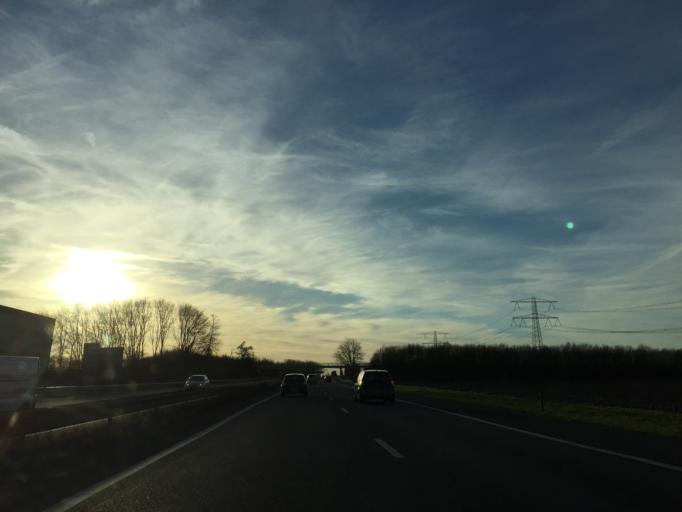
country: NL
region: South Holland
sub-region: Gemeente Binnenmaas
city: Mijnsheerenland
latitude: 51.8055
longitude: 4.4697
